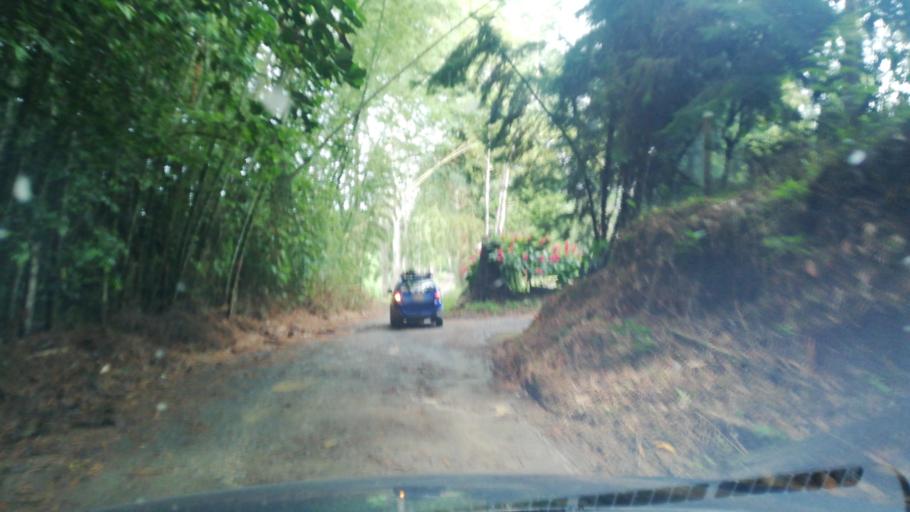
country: CO
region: Valle del Cauca
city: Restrepo
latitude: 3.8533
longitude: -76.4626
